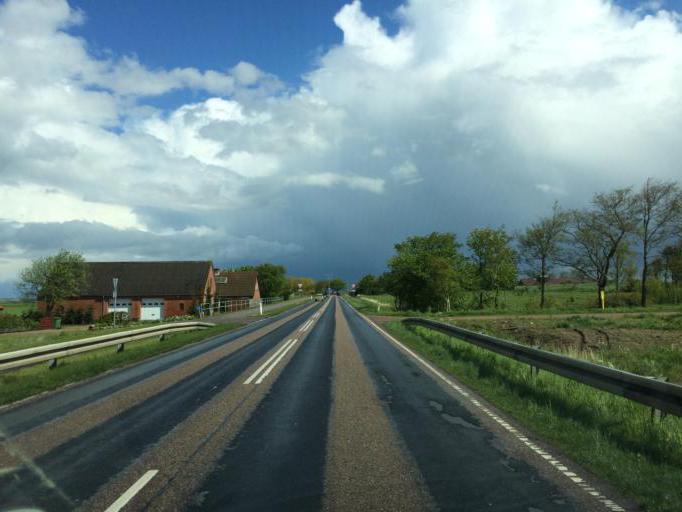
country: DK
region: Central Jutland
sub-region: Holstebro Kommune
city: Vinderup
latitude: 56.4656
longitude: 8.7701
